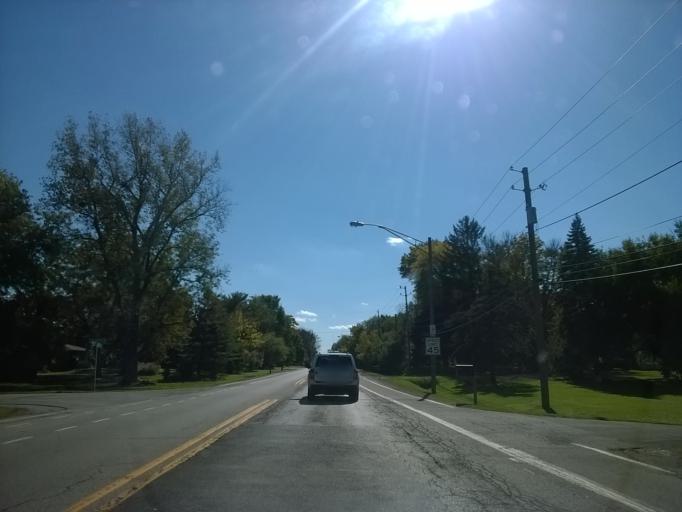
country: US
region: Indiana
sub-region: Marion County
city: Broad Ripple
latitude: 39.8663
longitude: -86.0982
